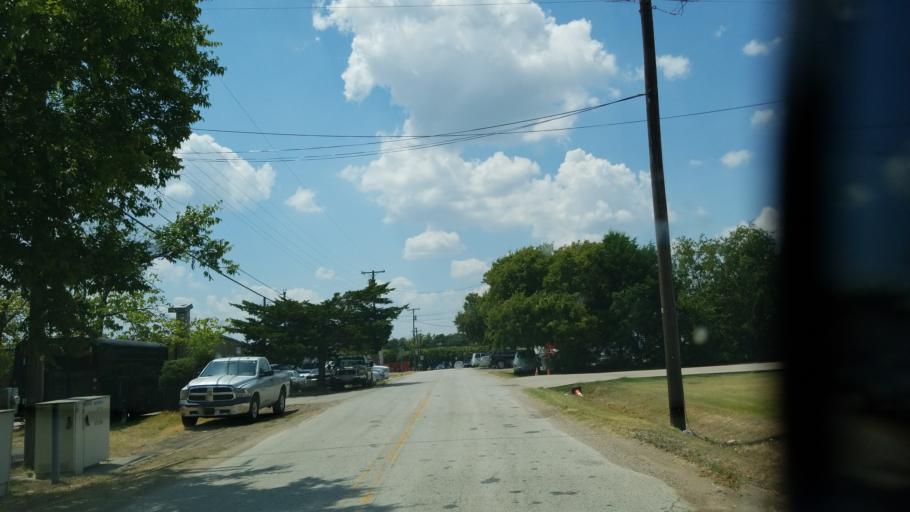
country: US
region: Texas
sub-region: Dallas County
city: Duncanville
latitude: 32.6742
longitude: -96.9021
